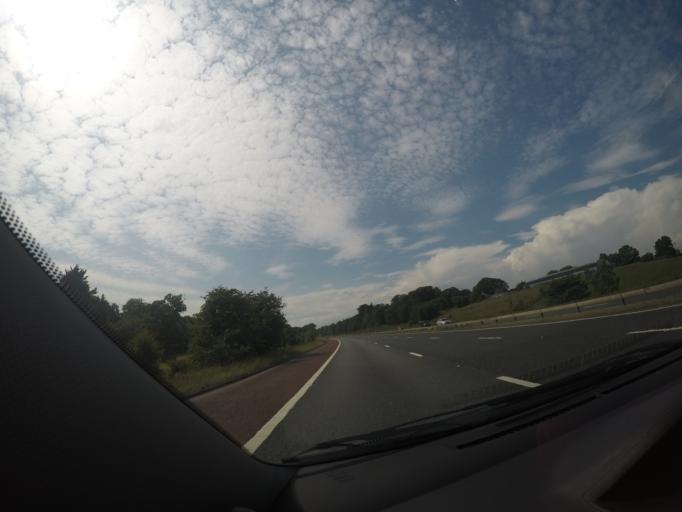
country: GB
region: England
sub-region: Cumbria
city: Carlisle
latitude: 54.9284
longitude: -2.9190
